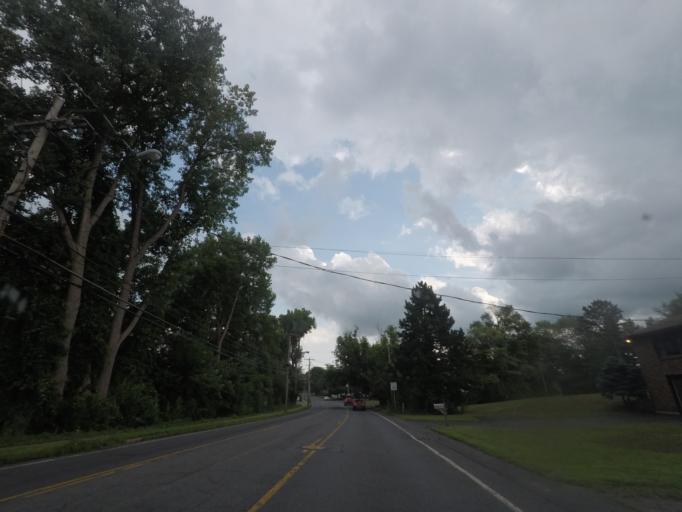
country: US
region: New York
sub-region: Albany County
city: Roessleville
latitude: 42.7084
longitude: -73.8037
